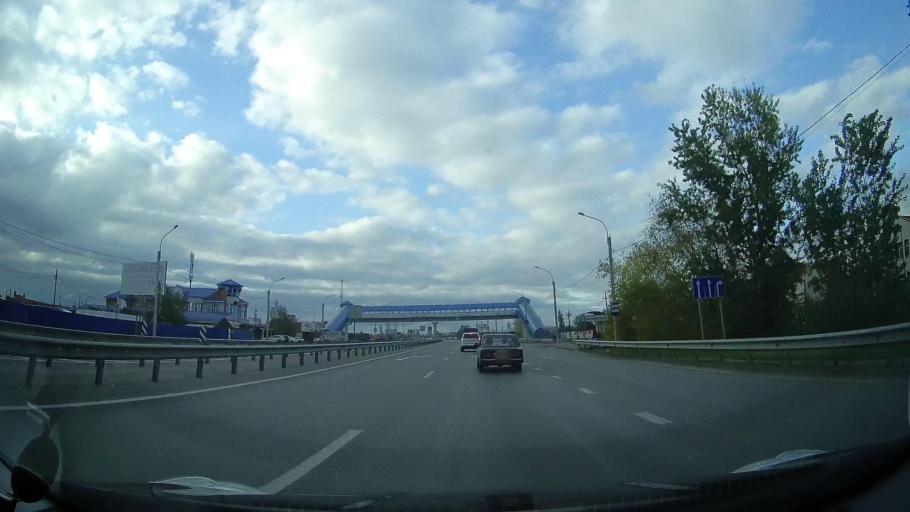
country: RU
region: Rostov
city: Bataysk
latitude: 47.1540
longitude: 39.7706
